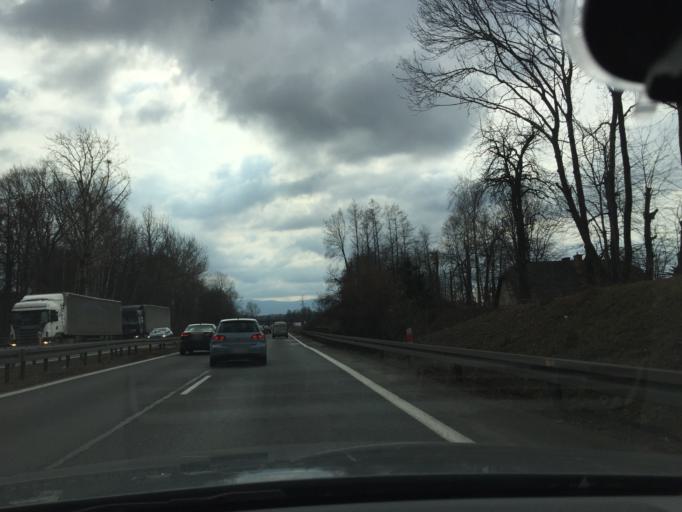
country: PL
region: Silesian Voivodeship
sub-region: Powiat bielski
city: Czechowice-Dziedzice
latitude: 49.9173
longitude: 18.9887
